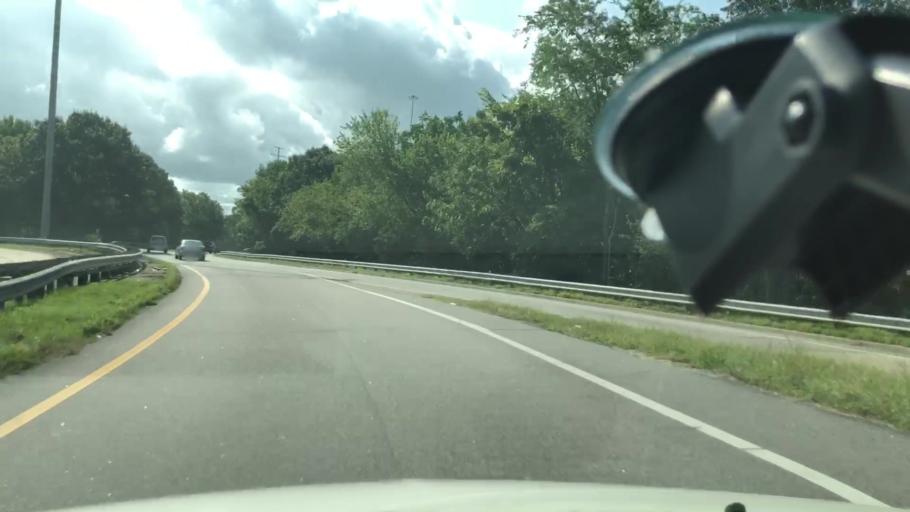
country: US
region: Virginia
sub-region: City of Chesapeake
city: Chesapeake
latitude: 36.8433
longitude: -76.1984
